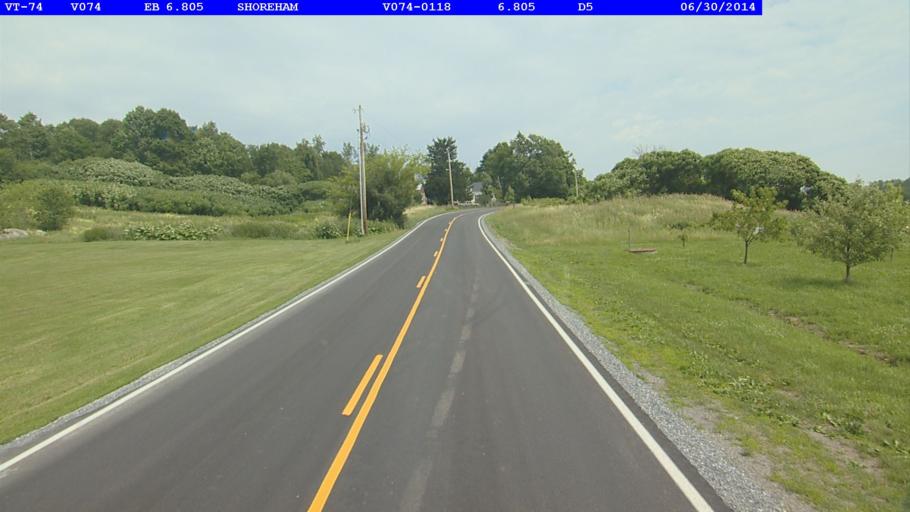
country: US
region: New York
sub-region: Essex County
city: Ticonderoga
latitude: 43.9176
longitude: -73.2955
